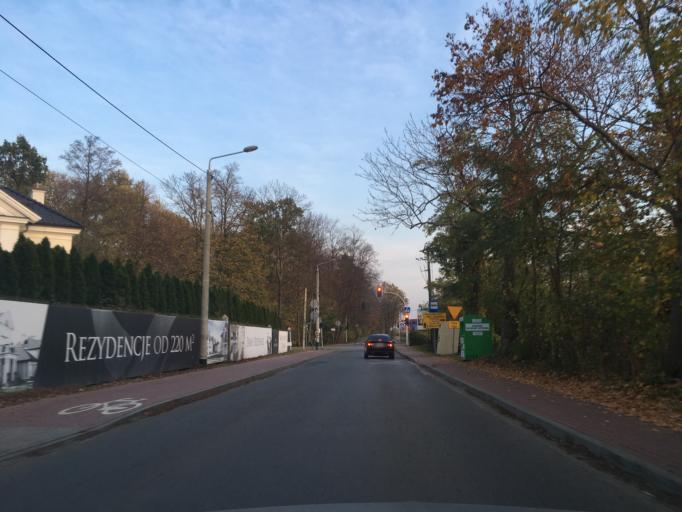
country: PL
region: Masovian Voivodeship
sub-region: Powiat pruszkowski
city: Nadarzyn
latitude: 52.0922
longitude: 20.8446
